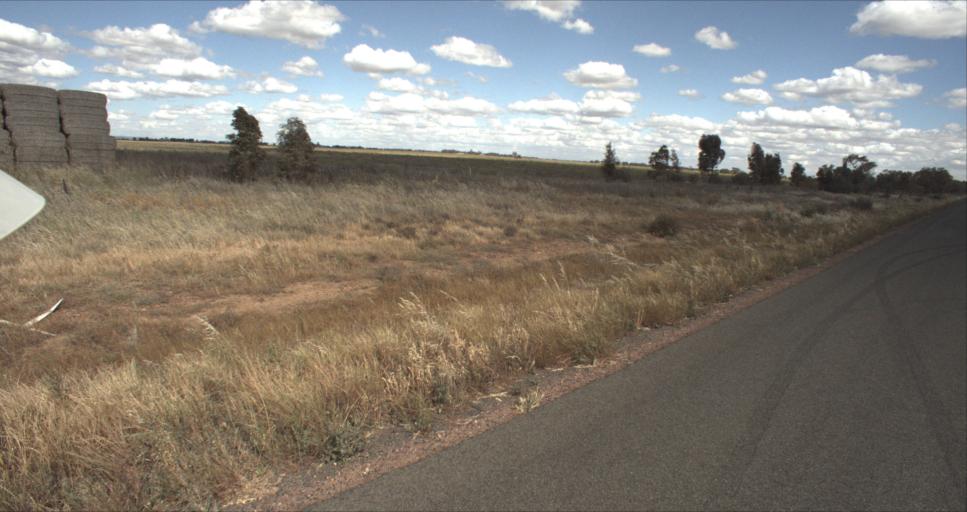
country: AU
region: New South Wales
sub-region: Leeton
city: Leeton
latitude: -34.4324
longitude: 146.2580
